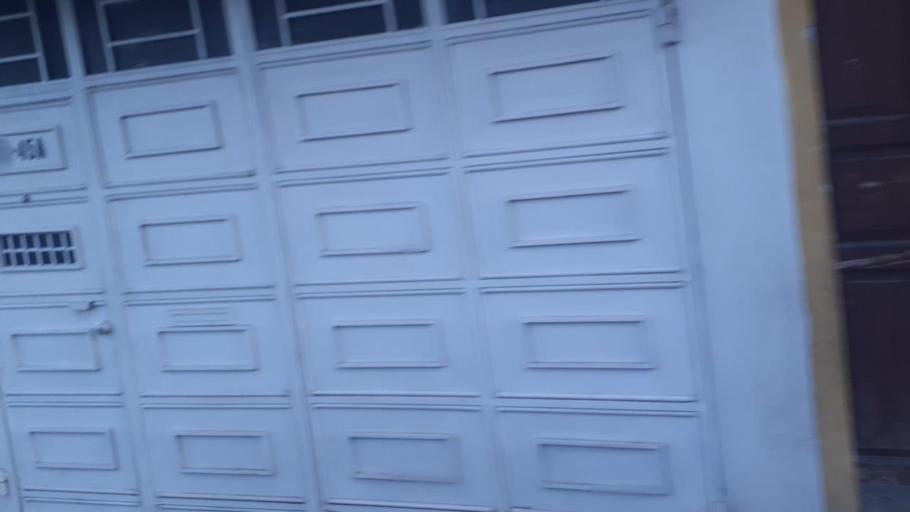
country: GT
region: Quetzaltenango
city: Quetzaltenango
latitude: 14.8342
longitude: -91.5253
